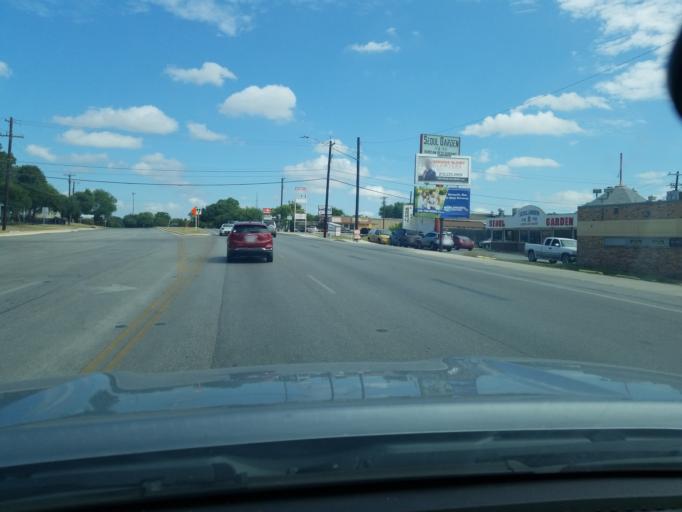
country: US
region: Texas
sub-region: Bexar County
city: Terrell Hills
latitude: 29.4860
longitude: -98.4300
